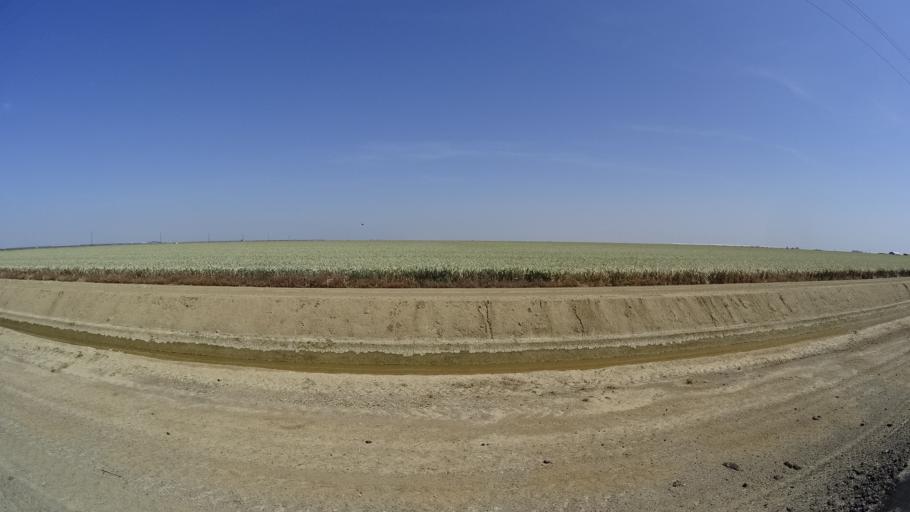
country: US
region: California
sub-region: Kings County
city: Kettleman City
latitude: 36.0941
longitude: -119.9470
